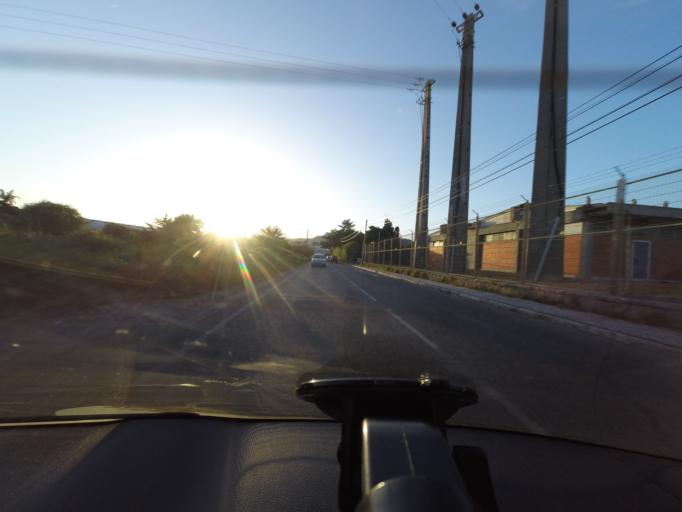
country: PT
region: Lisbon
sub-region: Sintra
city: Rio de Mouro
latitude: 38.7602
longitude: -9.3636
